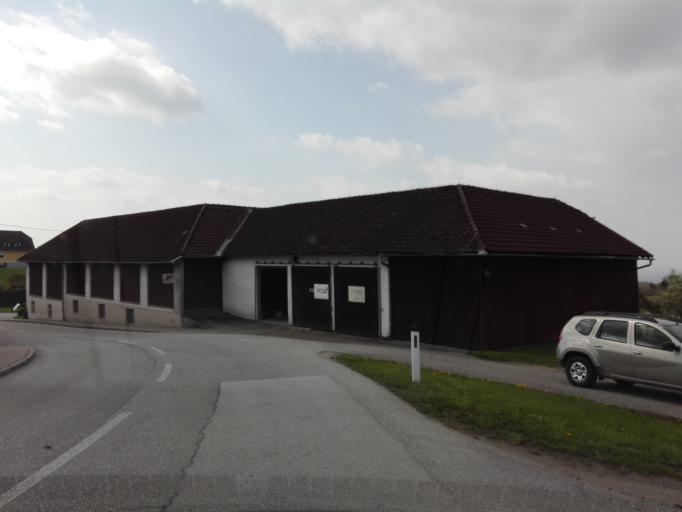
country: AT
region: Upper Austria
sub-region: Politischer Bezirk Perg
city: Perg
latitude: 48.2824
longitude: 14.6777
